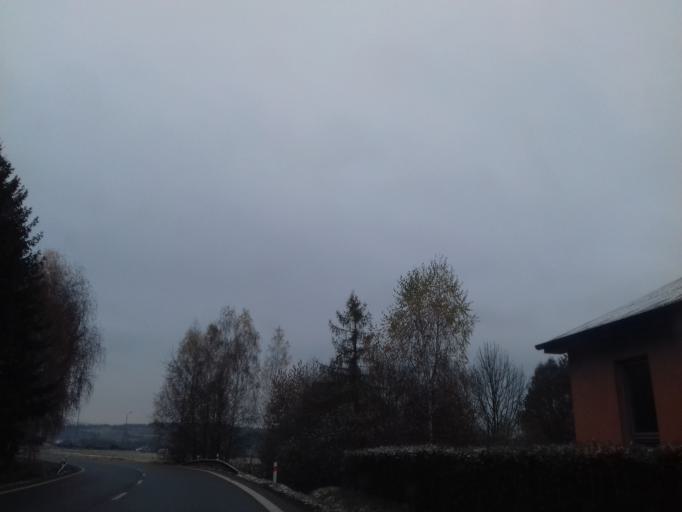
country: CZ
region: Plzensky
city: Meclov
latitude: 49.4563
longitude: 12.8703
